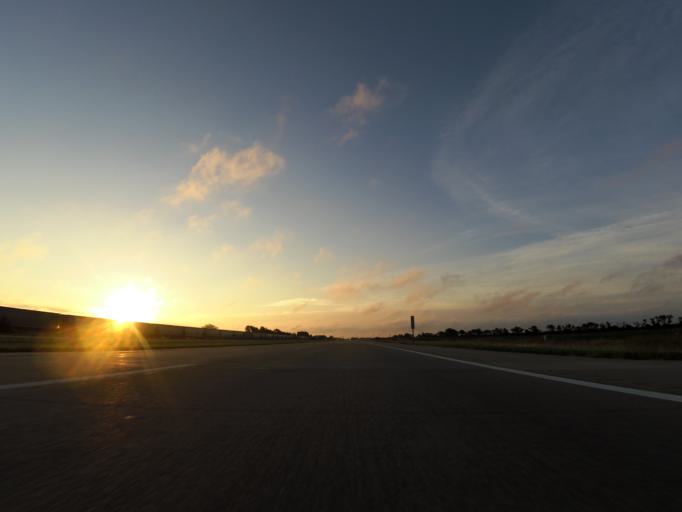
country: US
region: Kansas
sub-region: Reno County
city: South Hutchinson
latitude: 37.9512
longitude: -97.8946
